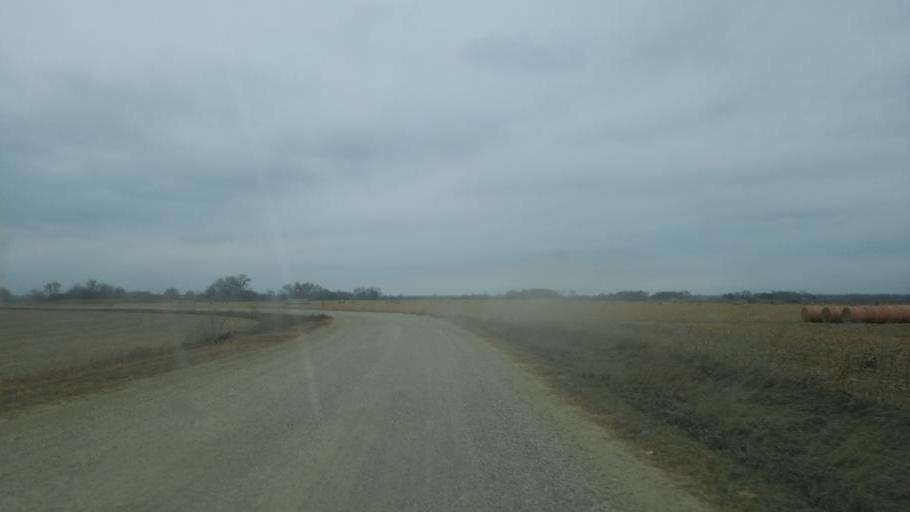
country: US
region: South Dakota
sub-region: Yankton County
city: Yankton
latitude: 42.8332
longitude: -97.3649
